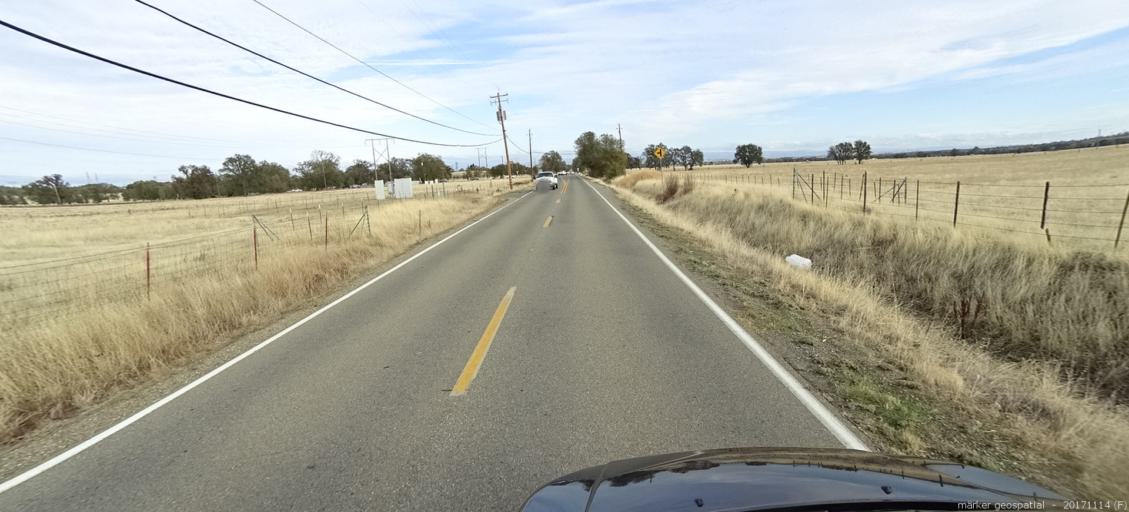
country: US
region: California
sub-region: Shasta County
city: Anderson
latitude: 40.3886
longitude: -122.4102
